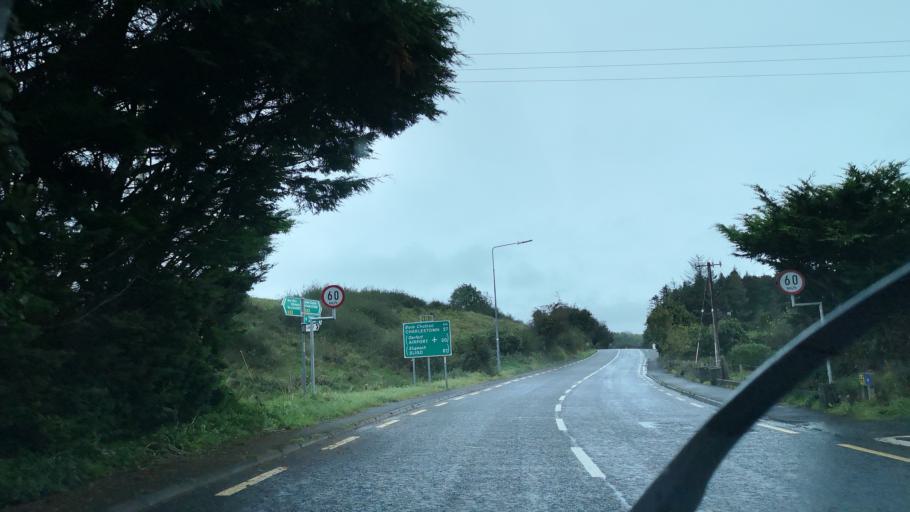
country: IE
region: Connaught
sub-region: Maigh Eo
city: Ballyhaunis
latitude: 53.7658
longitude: -8.7651
